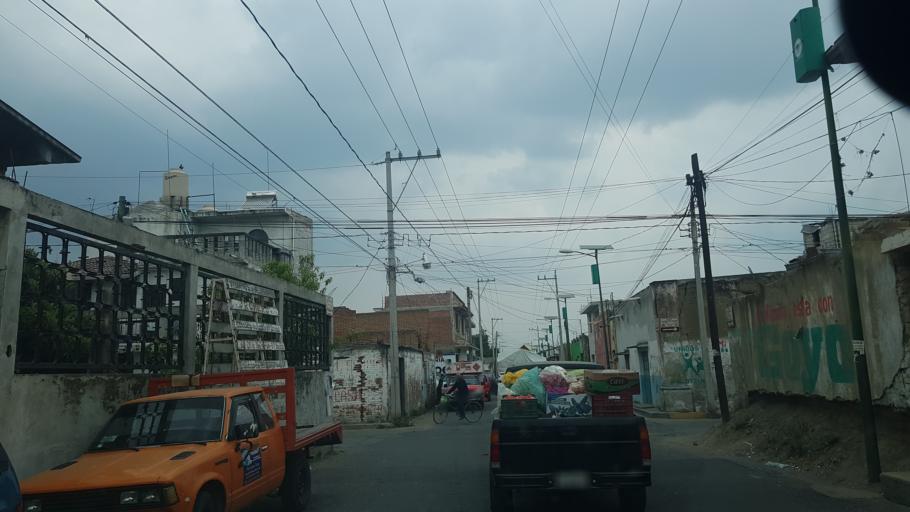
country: MX
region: Puebla
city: Huejotzingo
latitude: 19.1646
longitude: -98.4117
